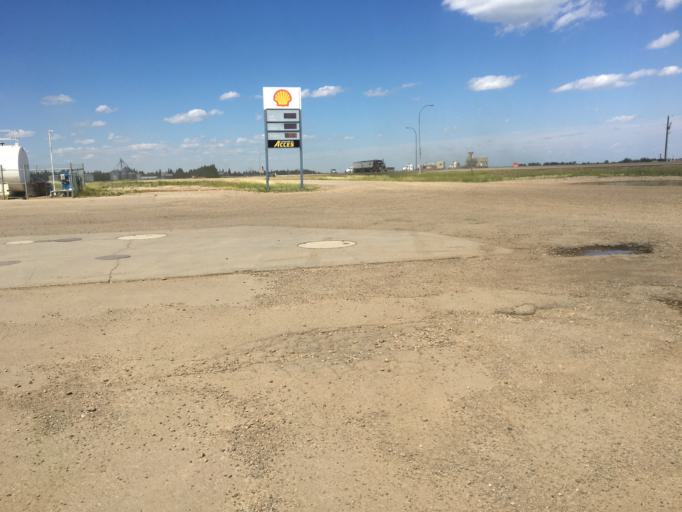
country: CA
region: Alberta
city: Spirit River
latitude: 55.7574
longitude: -118.6995
